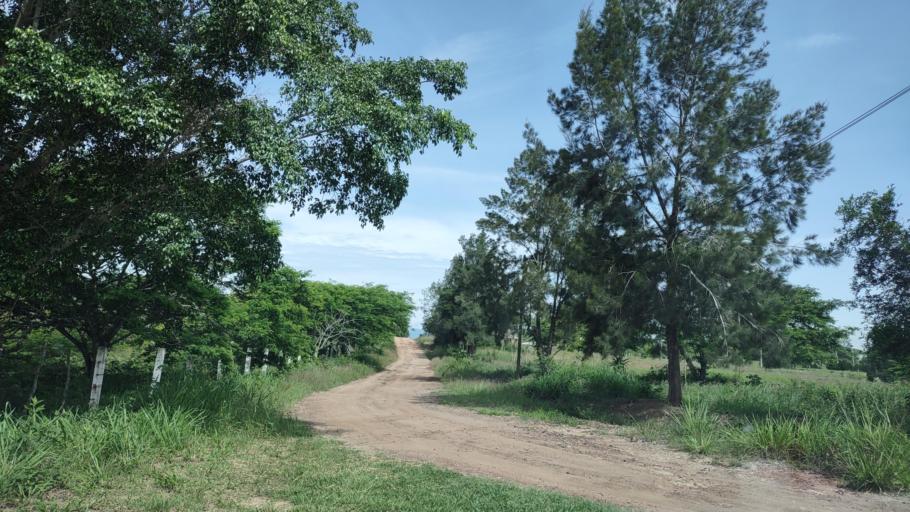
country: MX
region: Veracruz
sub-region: Emiliano Zapata
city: Dos Rios
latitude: 19.4701
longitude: -96.8257
